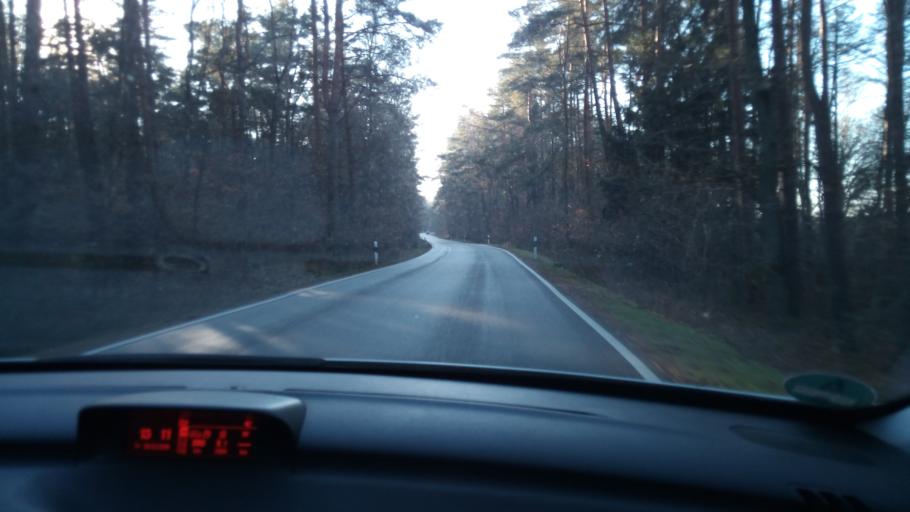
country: DE
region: Schleswig-Holstein
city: Gottin
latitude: 53.5157
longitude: 10.6986
